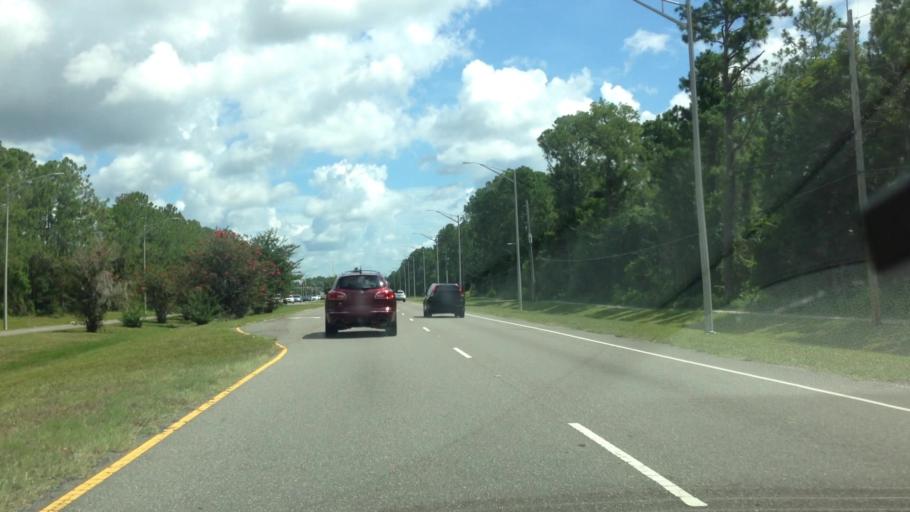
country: US
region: Florida
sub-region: Duval County
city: Jacksonville Beach
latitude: 30.2799
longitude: -81.4604
